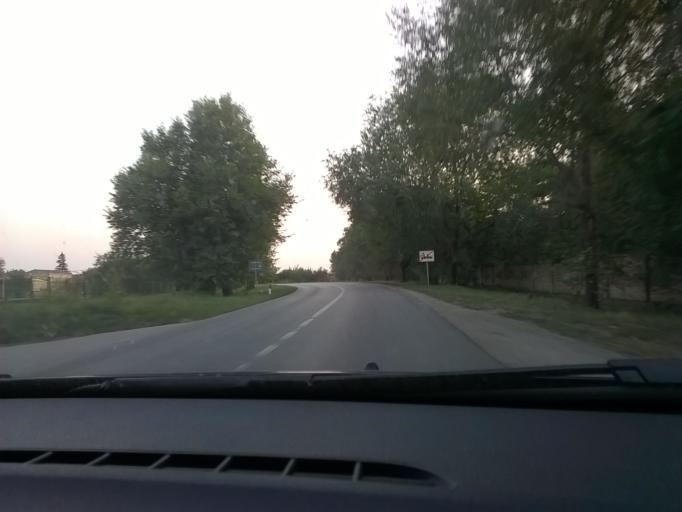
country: RS
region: Autonomna Pokrajina Vojvodina
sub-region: Juznobanatski Okrug
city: Vrsac
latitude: 45.1078
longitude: 21.2977
